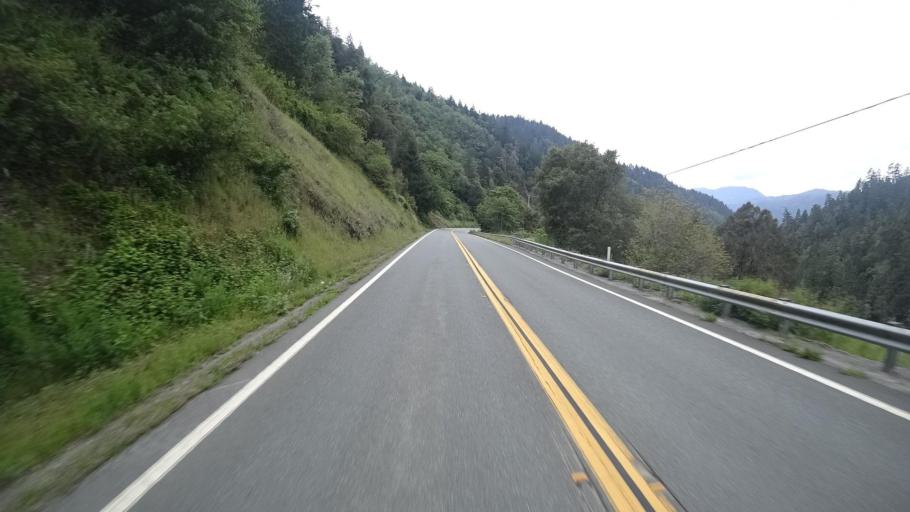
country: US
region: California
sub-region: Humboldt County
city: Willow Creek
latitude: 41.1131
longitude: -123.6872
